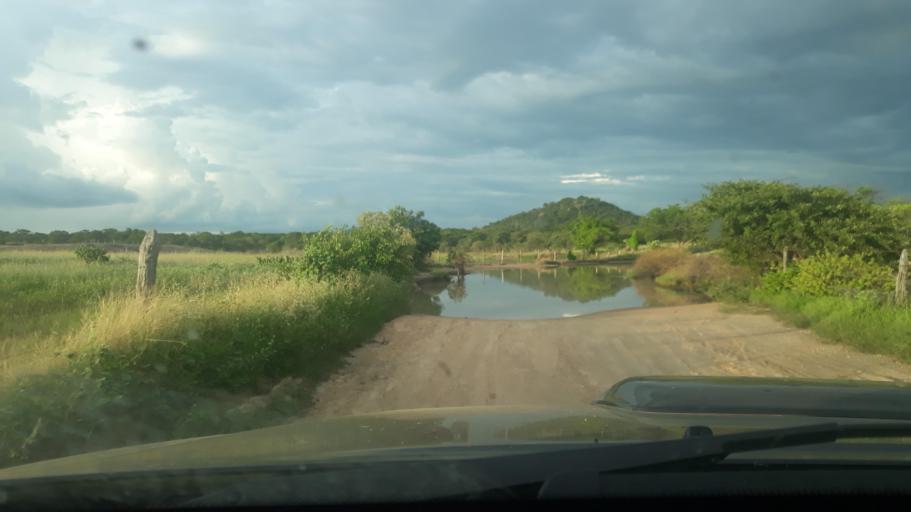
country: BR
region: Bahia
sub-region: Riacho De Santana
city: Riacho de Santana
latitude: -13.9101
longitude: -42.9467
